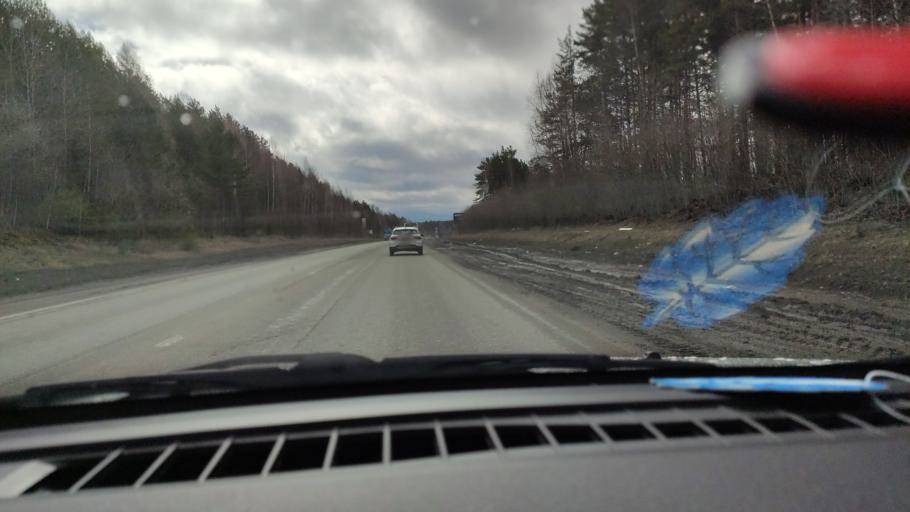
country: RU
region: Sverdlovsk
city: Talitsa
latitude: 56.8685
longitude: 60.0432
